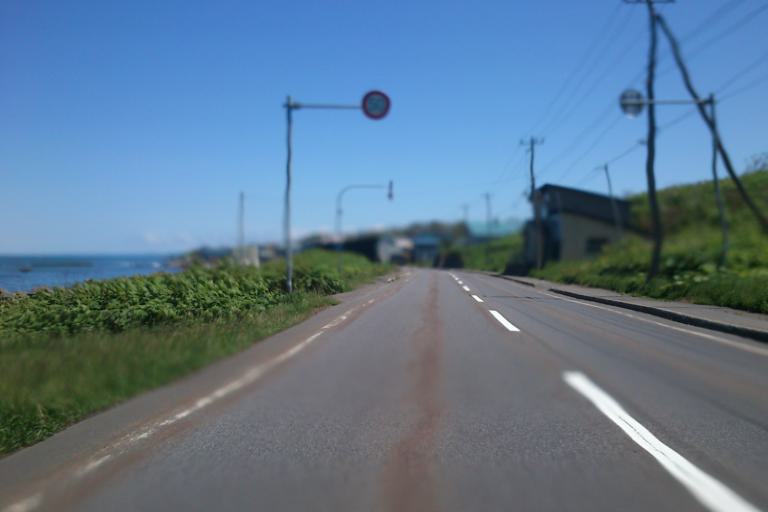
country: JP
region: Hokkaido
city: Rumoi
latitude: 43.8372
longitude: 141.4959
